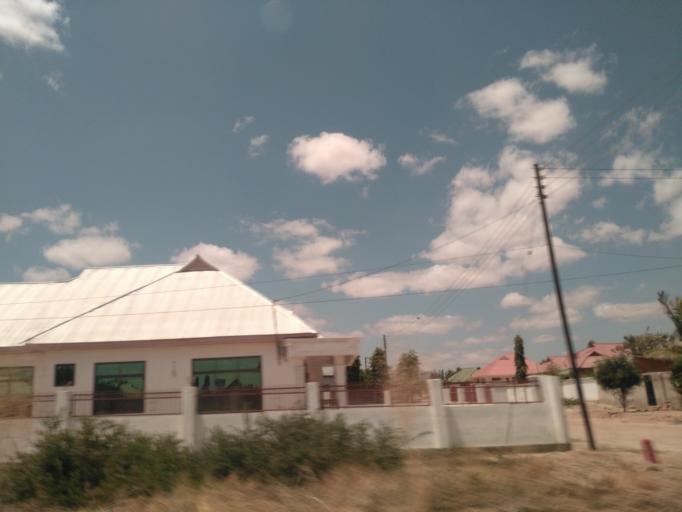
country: TZ
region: Dodoma
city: Kisasa
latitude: -6.1651
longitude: 35.7955
